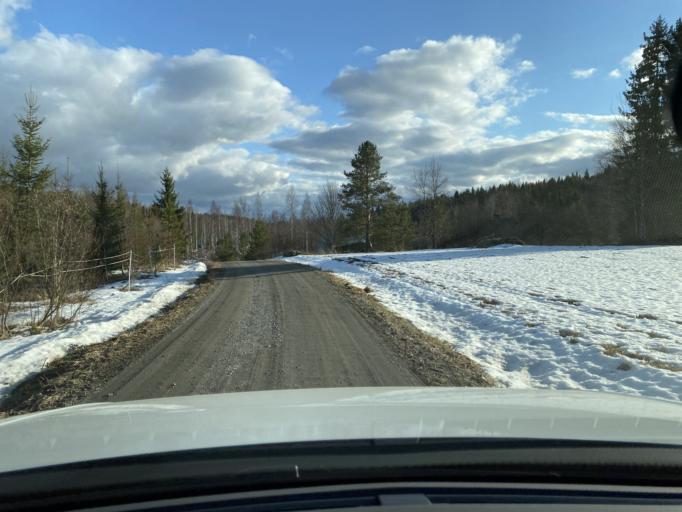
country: FI
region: Pirkanmaa
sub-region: Lounais-Pirkanmaa
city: Mouhijaervi
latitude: 61.4578
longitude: 22.9586
